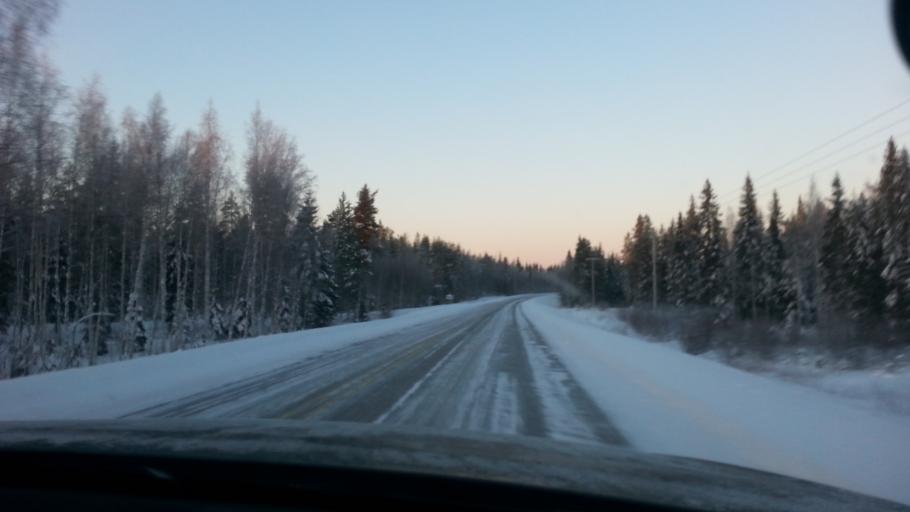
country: FI
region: Lapland
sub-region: Rovaniemi
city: Rovaniemi
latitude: 66.7893
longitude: 25.4389
